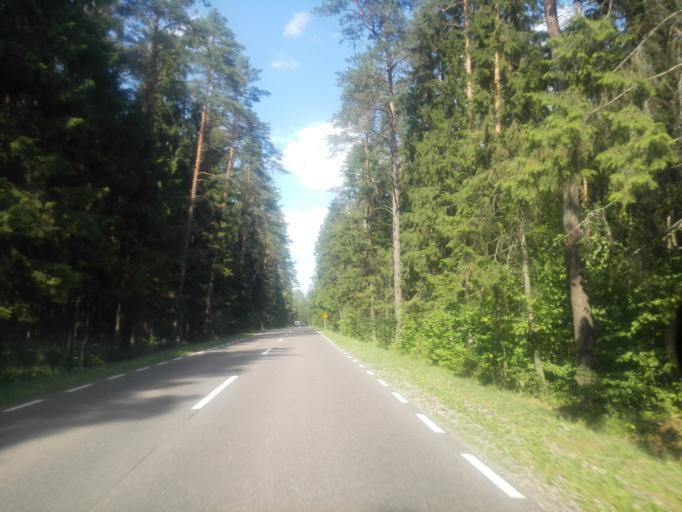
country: PL
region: Podlasie
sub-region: Powiat sejnenski
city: Krasnopol
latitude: 53.9344
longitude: 23.1673
